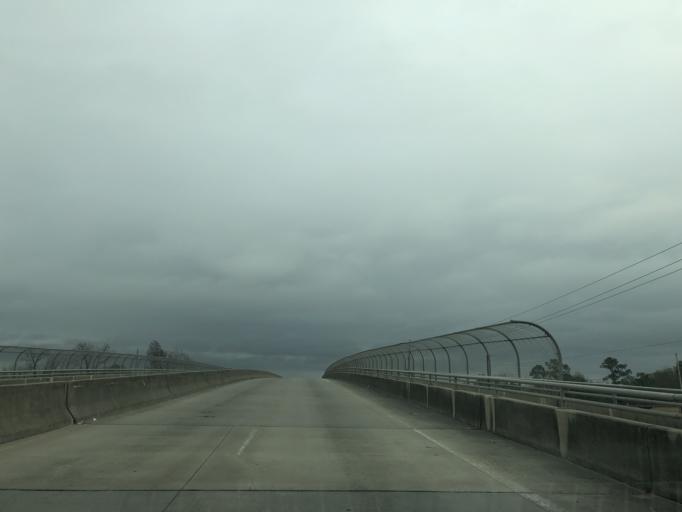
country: US
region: Texas
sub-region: Harris County
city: Jacinto City
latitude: 29.8313
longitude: -95.2901
